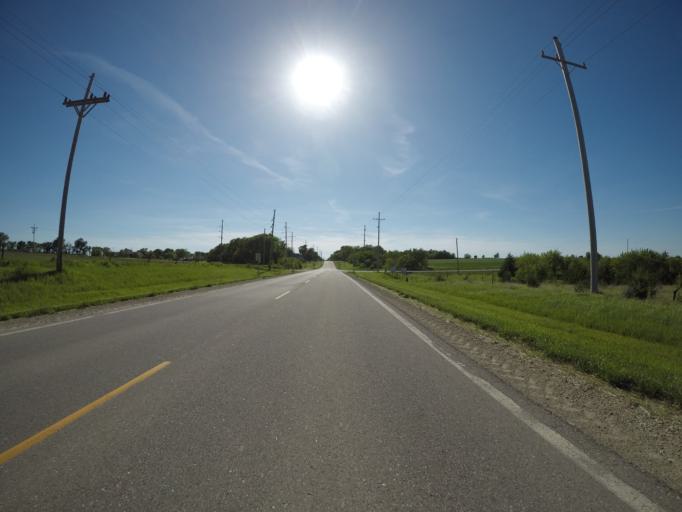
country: US
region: Kansas
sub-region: Riley County
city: Fort Riley North
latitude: 39.3645
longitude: -96.8484
